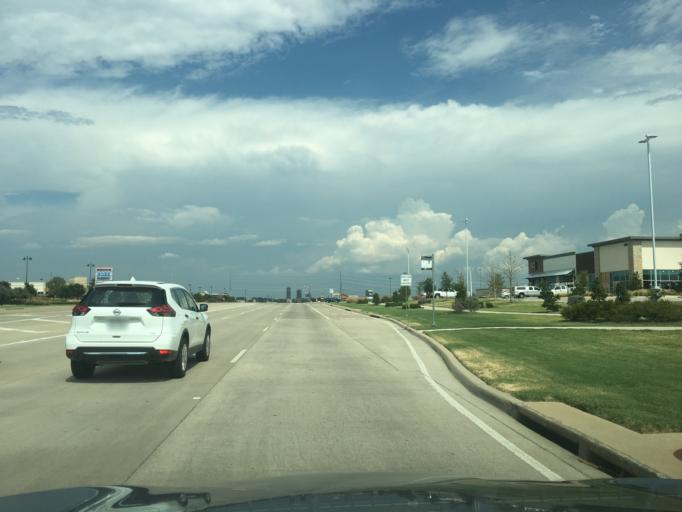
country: US
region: Texas
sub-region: Denton County
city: Denton
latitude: 33.2297
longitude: -97.1664
